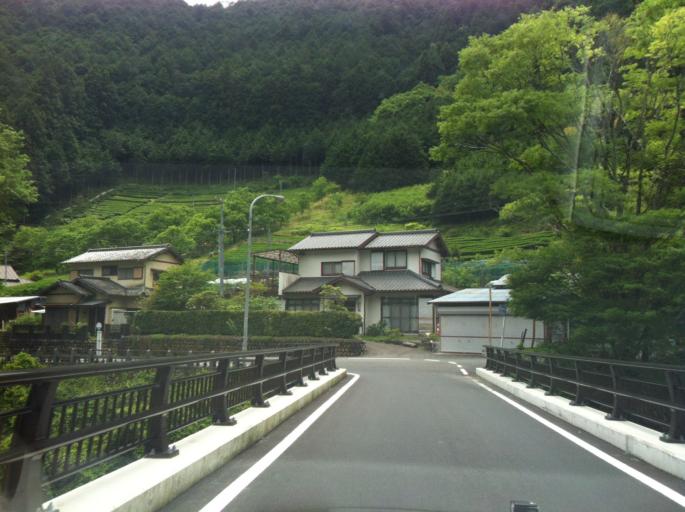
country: JP
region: Shizuoka
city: Shizuoka-shi
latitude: 35.1289
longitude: 138.3233
